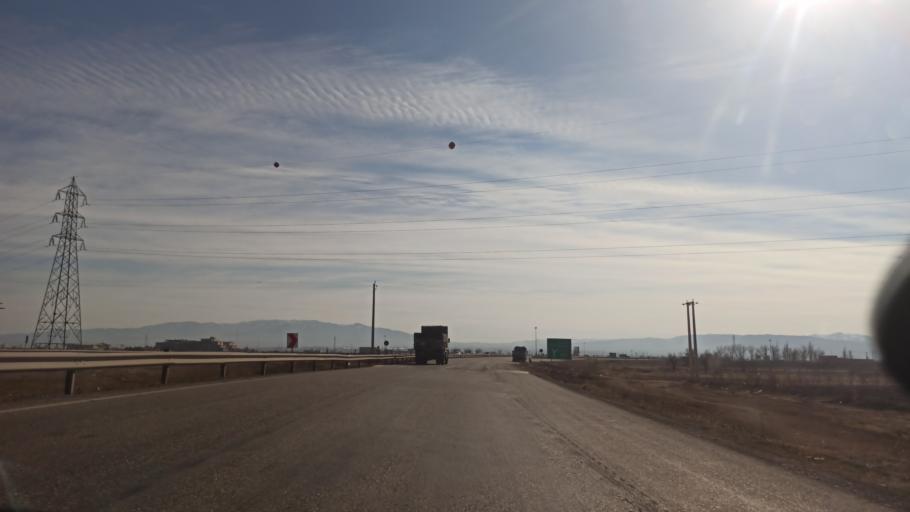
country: IR
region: Qazvin
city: Bu'in Zahra
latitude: 35.7726
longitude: 50.0854
